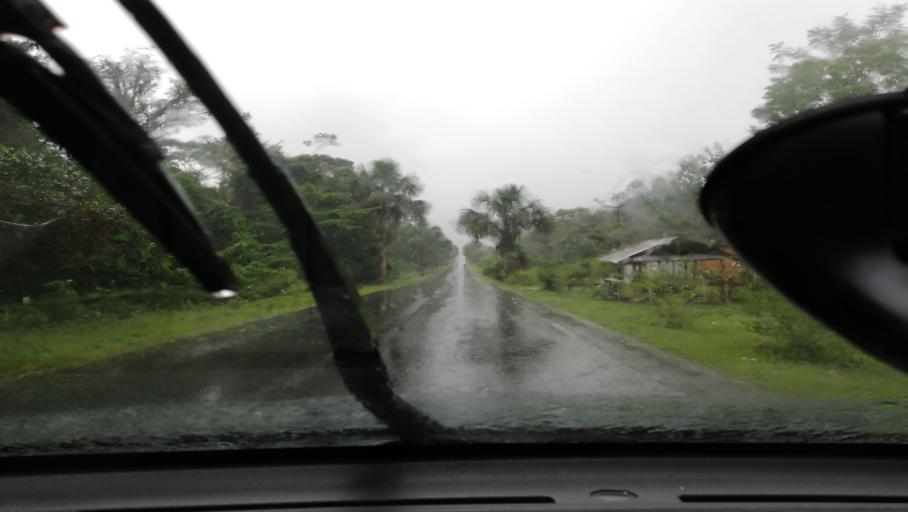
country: PE
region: Loreto
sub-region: Provincia de Maynas
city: San Juan
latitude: -3.9621
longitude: -73.4143
